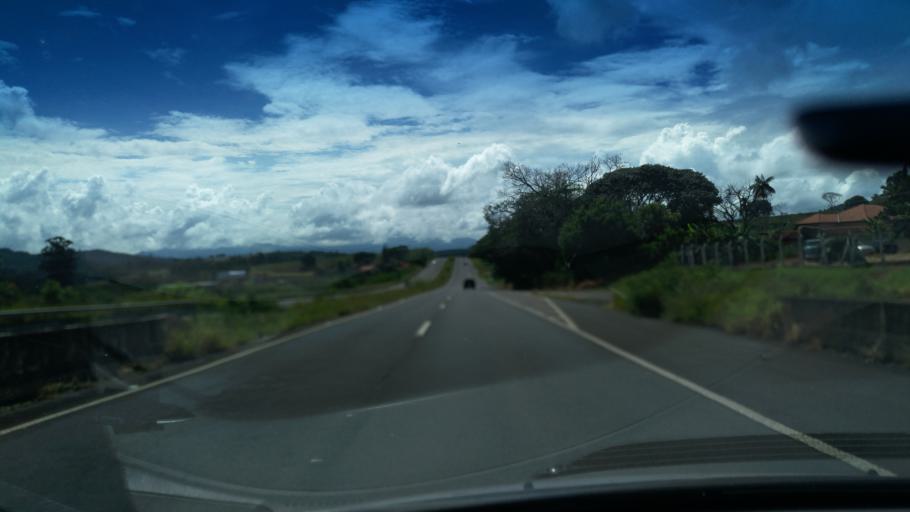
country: BR
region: Sao Paulo
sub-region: Santo Antonio Do Jardim
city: Espirito Santo do Pinhal
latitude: -22.1742
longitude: -46.7471
